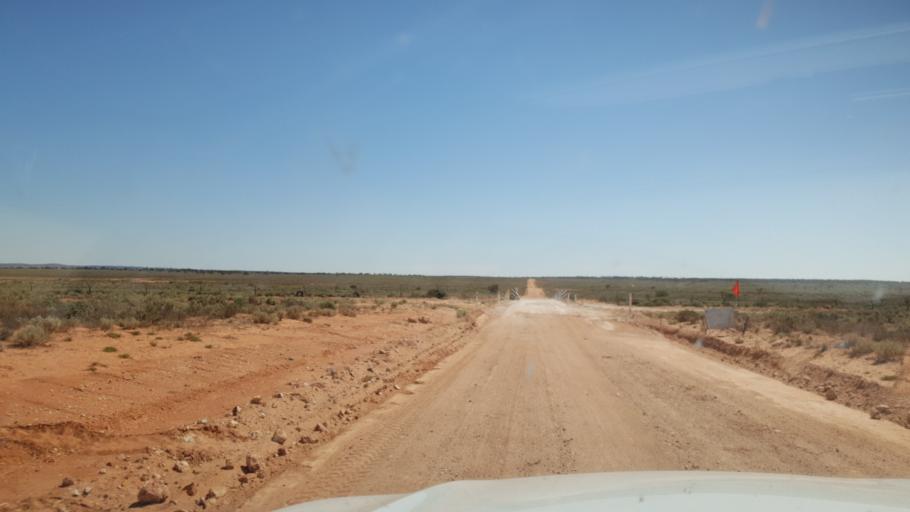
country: AU
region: South Australia
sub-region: Whyalla
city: Whyalla
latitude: -32.6368
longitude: 136.9113
